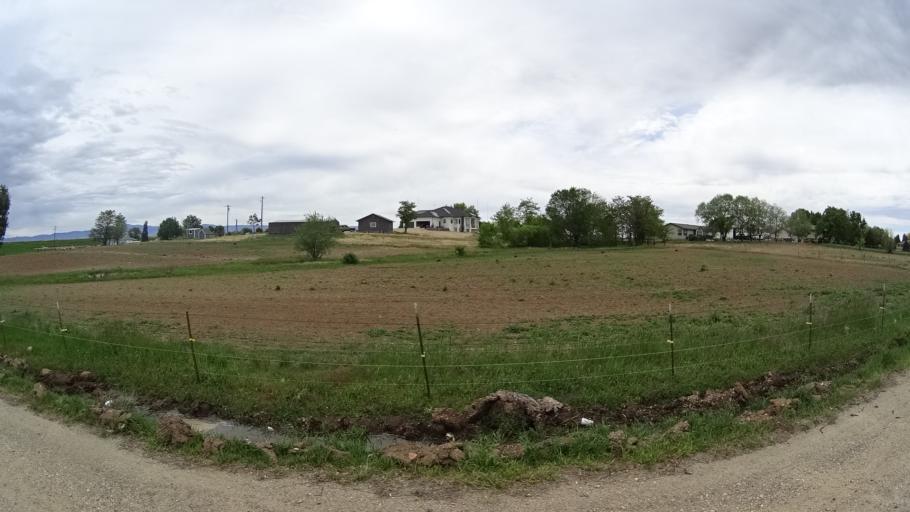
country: US
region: Idaho
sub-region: Ada County
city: Meridian
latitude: 43.5595
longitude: -116.4138
